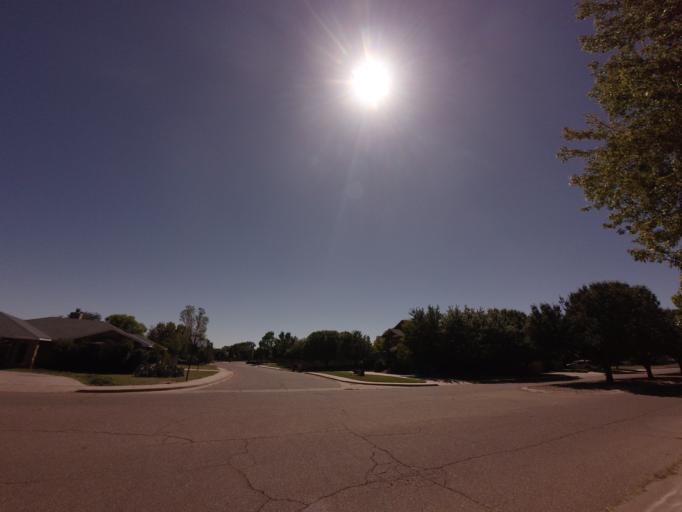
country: US
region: New Mexico
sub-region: Curry County
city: Clovis
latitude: 34.4458
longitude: -103.1814
